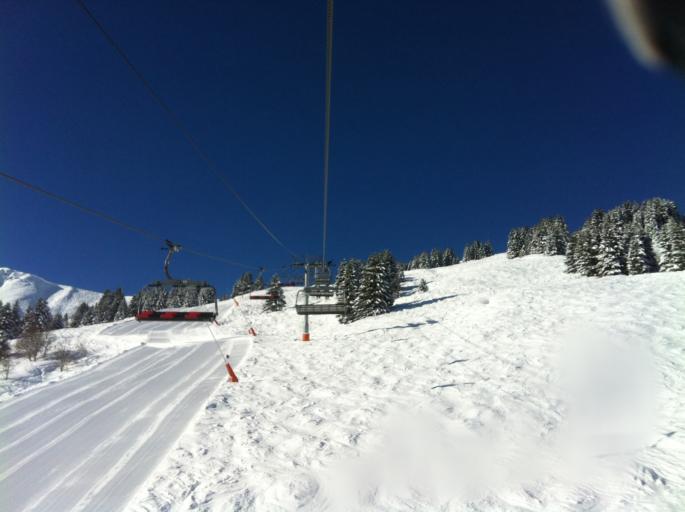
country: FR
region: Rhone-Alpes
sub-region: Departement de la Haute-Savoie
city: Les Contamines-Montjoie
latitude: 45.8489
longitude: 6.6935
